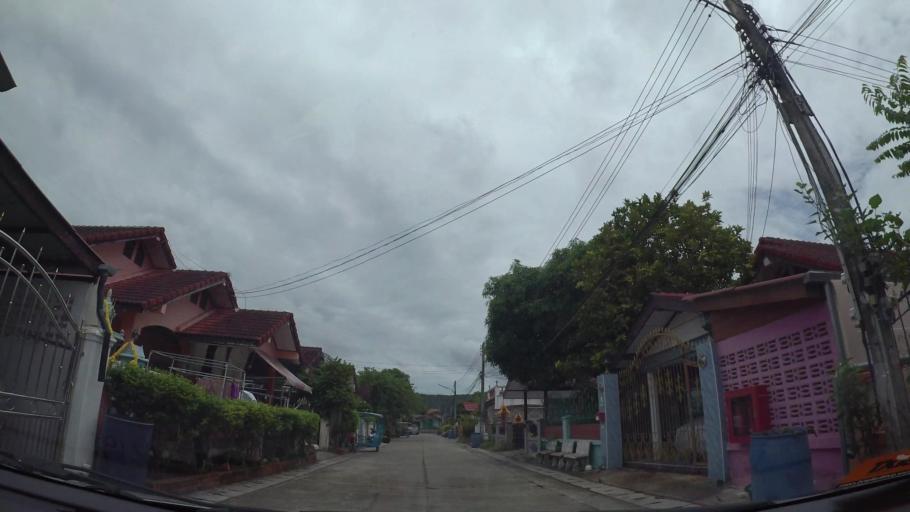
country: TH
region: Chon Buri
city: Sattahip
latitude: 12.7591
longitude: 100.8944
